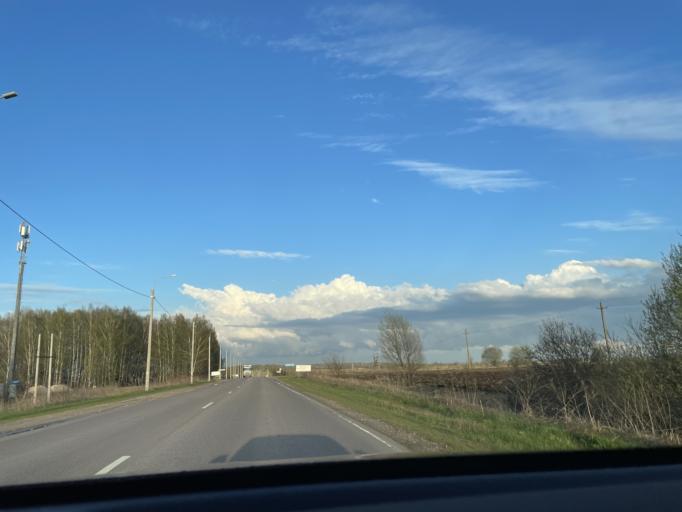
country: RU
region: Tula
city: Novogurovskiy
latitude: 54.5263
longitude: 37.4086
